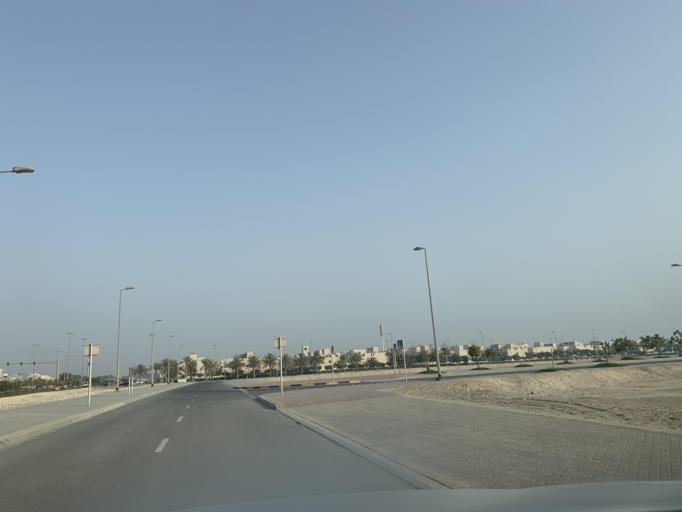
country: BH
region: Manama
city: Jidd Hafs
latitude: 26.2287
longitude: 50.4483
